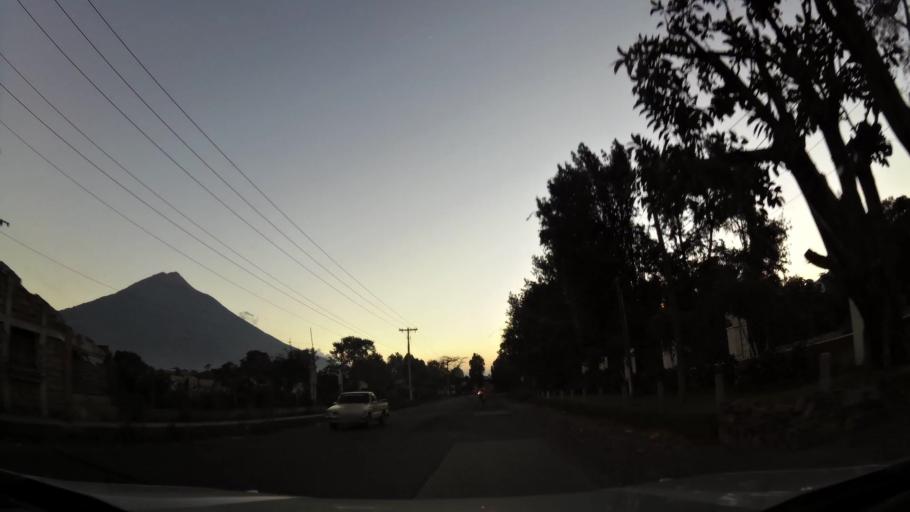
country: GT
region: Sacatepequez
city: Antigua Guatemala
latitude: 14.5483
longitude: -90.7437
